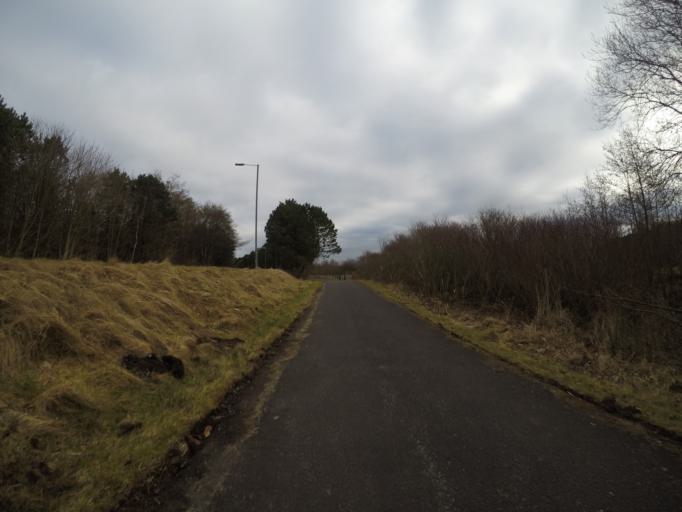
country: GB
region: Scotland
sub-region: North Ayrshire
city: Irvine
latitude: 55.5905
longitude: -4.6583
